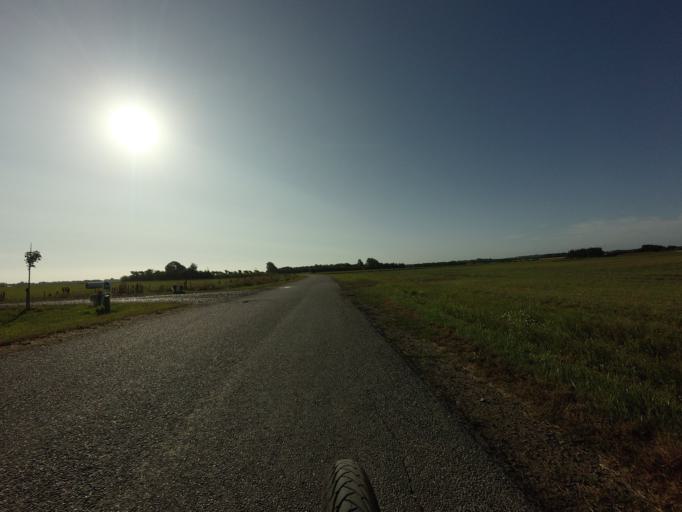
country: DK
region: North Denmark
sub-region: Hjorring Kommune
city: Vra
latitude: 57.3918
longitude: 9.9298
